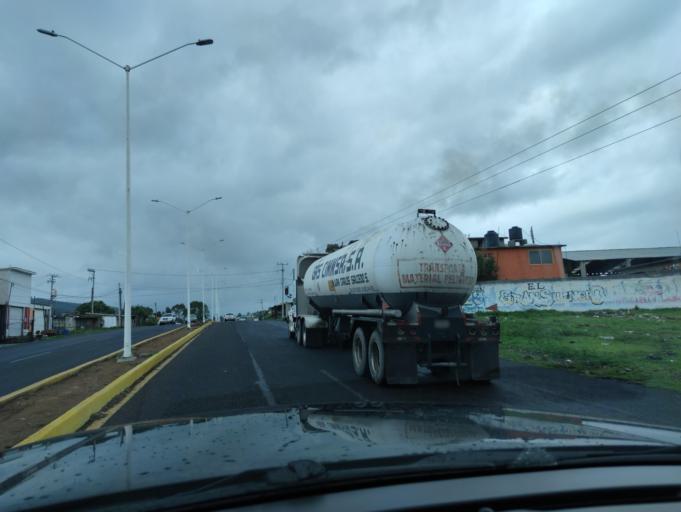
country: MX
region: Mexico
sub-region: Jilotepec
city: Octeyuco Dos Mil
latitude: 19.8873
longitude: -99.6438
